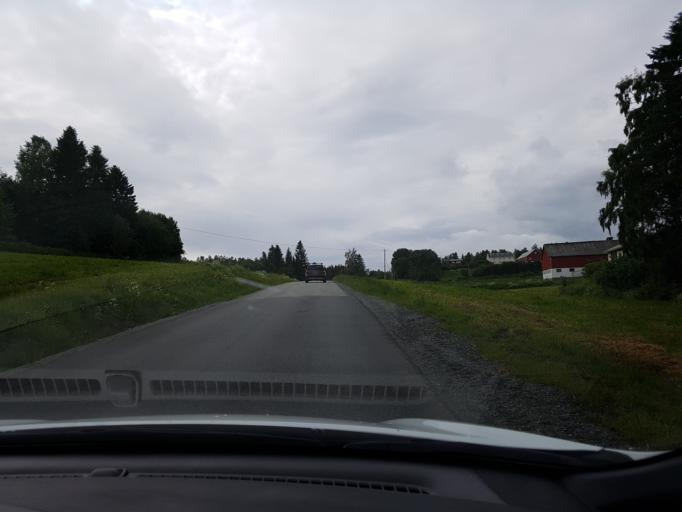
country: NO
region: Nord-Trondelag
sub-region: Frosta
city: Frosta
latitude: 63.6170
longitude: 10.7543
